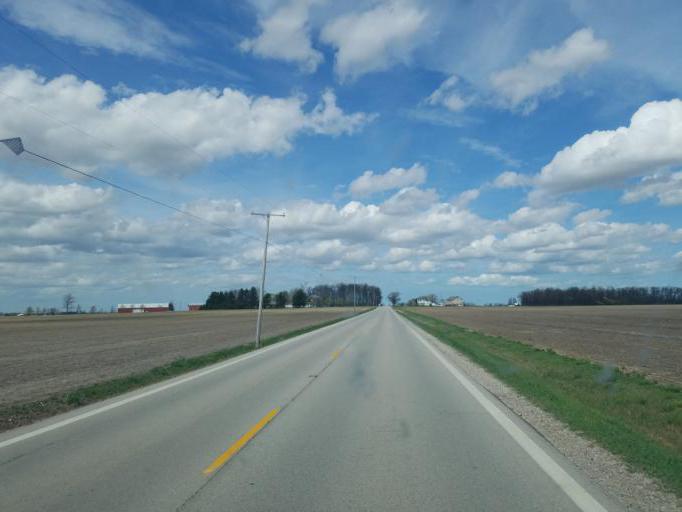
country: US
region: Ohio
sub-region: Huron County
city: Bellevue
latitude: 41.2428
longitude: -82.8050
